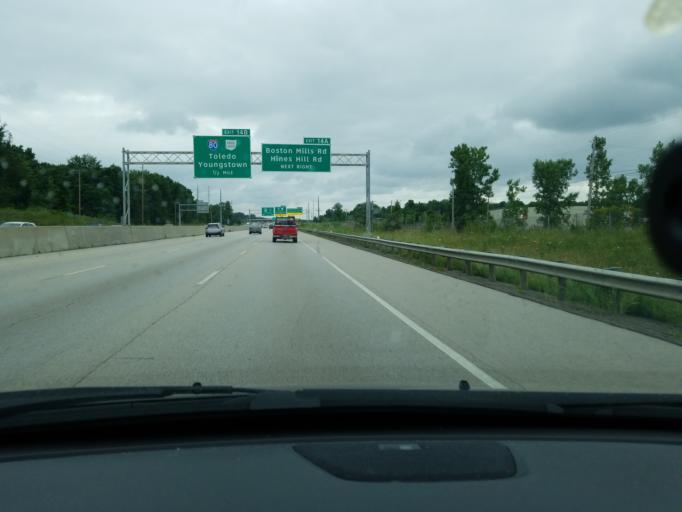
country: US
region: Ohio
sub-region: Summit County
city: Boston Heights
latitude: 41.2454
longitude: -81.4967
